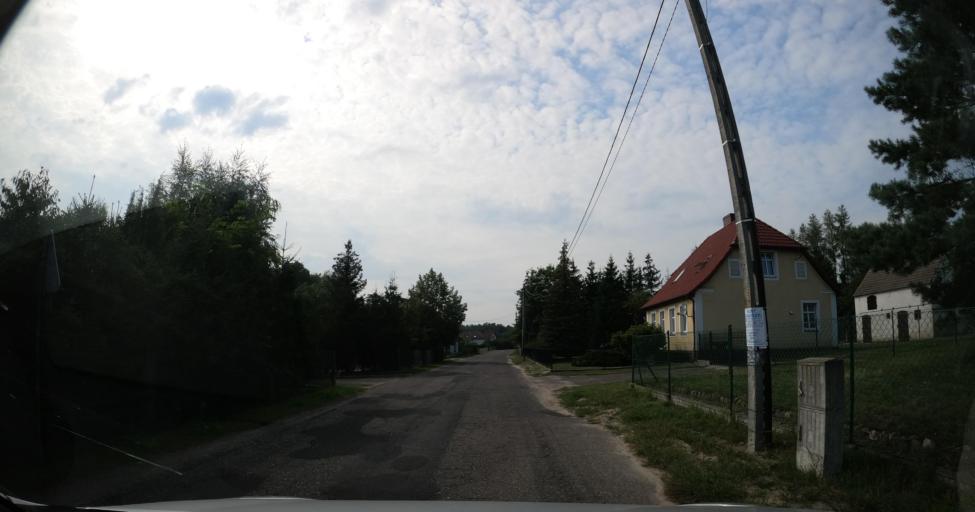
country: PL
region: West Pomeranian Voivodeship
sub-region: Powiat goleniowski
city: Goleniow
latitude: 53.5041
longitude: 14.8794
